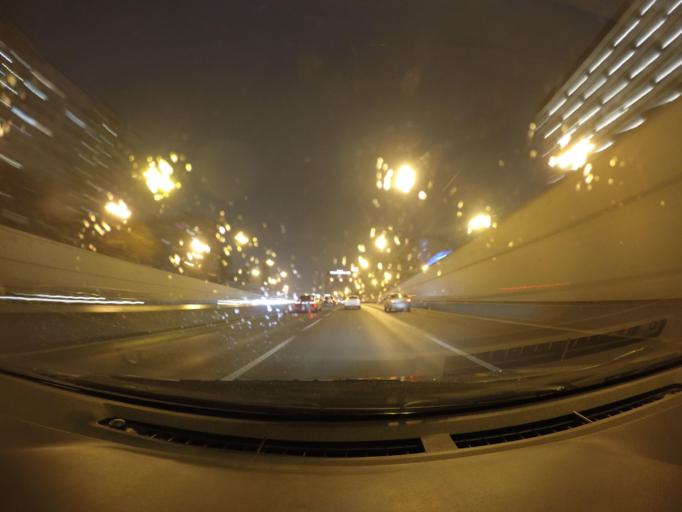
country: RU
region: Moscow
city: Lefortovo
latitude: 55.7758
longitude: 37.6829
